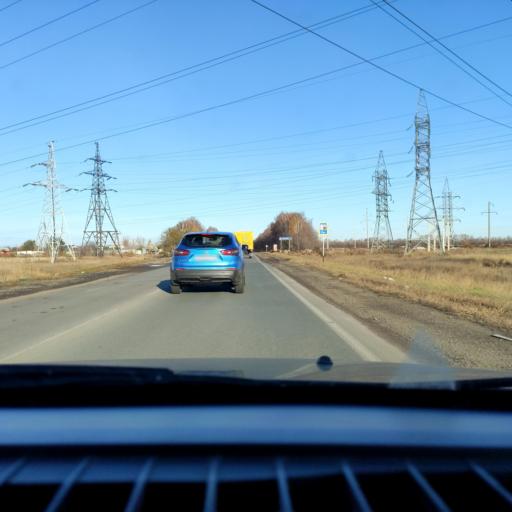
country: RU
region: Samara
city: Tol'yatti
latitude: 53.5868
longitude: 49.3318
